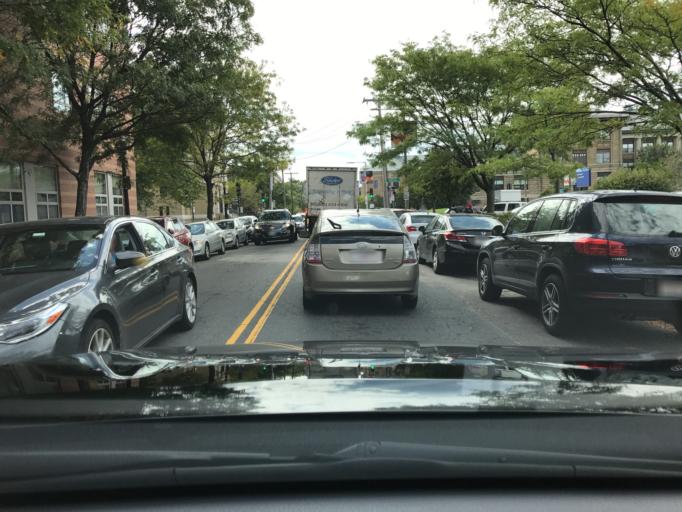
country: US
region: Massachusetts
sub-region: Norfolk County
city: Brookline
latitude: 42.3375
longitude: -71.0933
